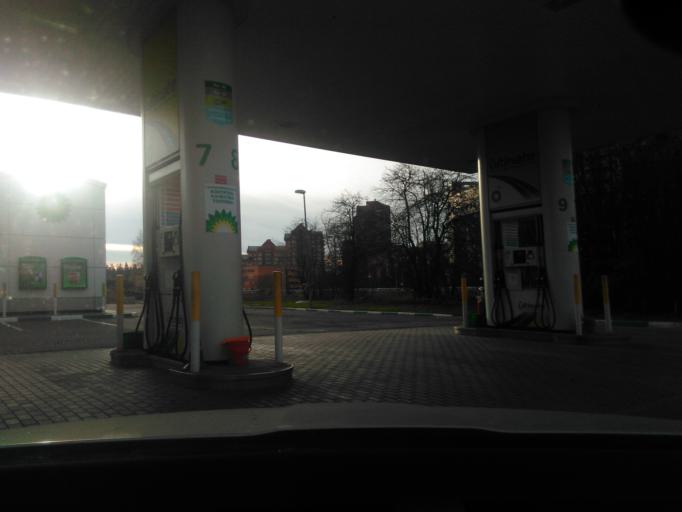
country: RU
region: Moskovskaya
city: Rzhavki
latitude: 55.9952
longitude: 37.2539
